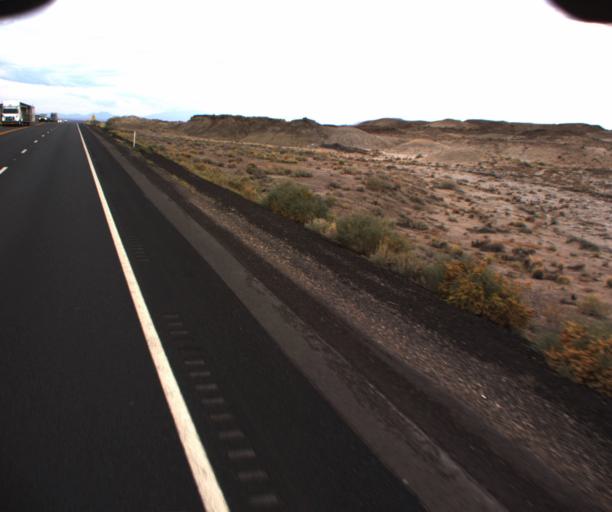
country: US
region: Arizona
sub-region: Coconino County
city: Tuba City
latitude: 36.0618
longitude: -111.3941
